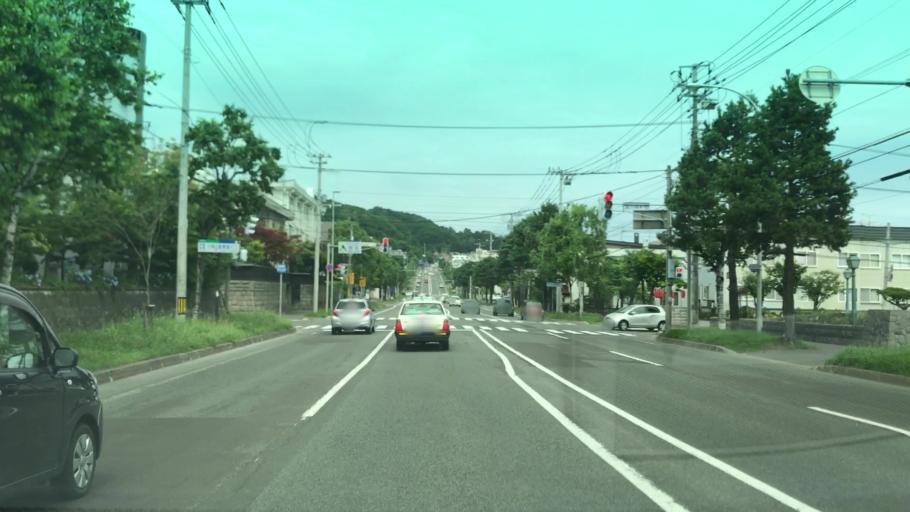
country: JP
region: Hokkaido
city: Sapporo
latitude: 43.0606
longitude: 141.2968
